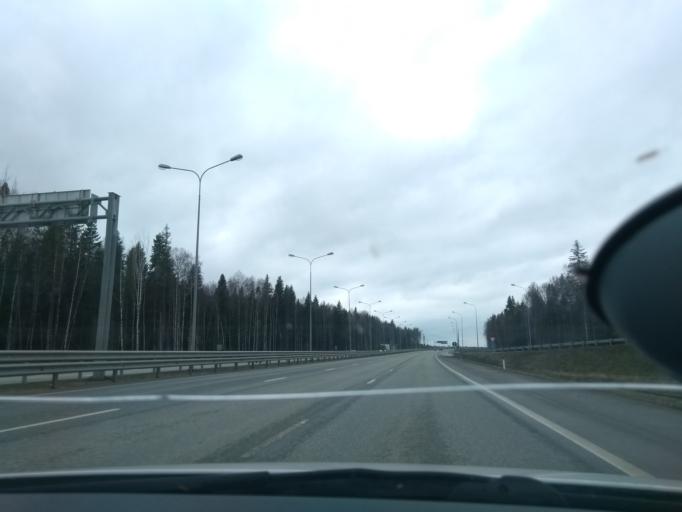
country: RU
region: Perm
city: Bershet'
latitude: 57.6992
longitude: 56.3805
